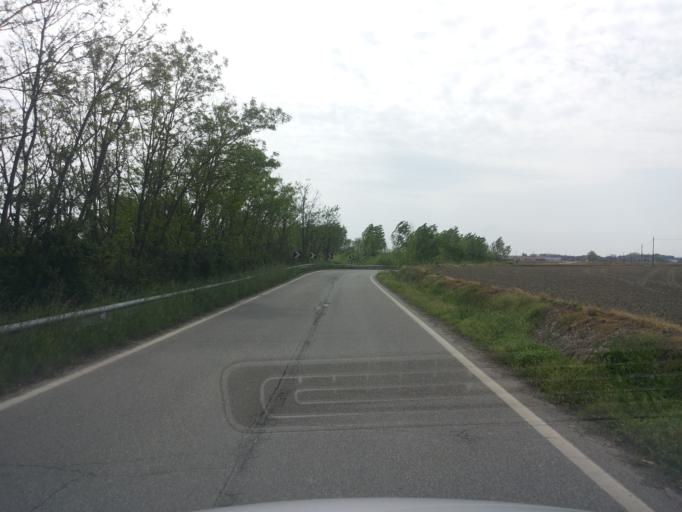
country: IT
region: Piedmont
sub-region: Provincia di Vercelli
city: Motta De Conti
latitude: 45.2053
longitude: 8.5153
